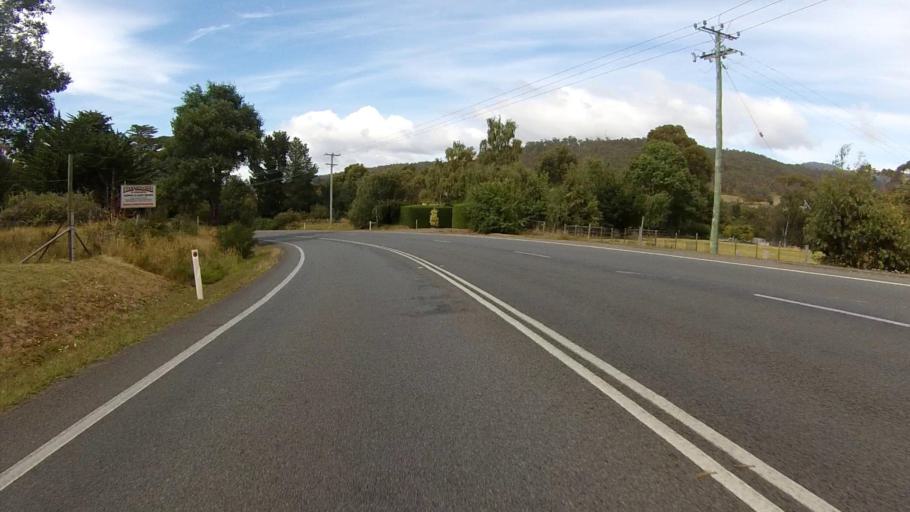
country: AU
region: Tasmania
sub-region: Kingborough
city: Kettering
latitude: -43.1187
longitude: 147.2438
